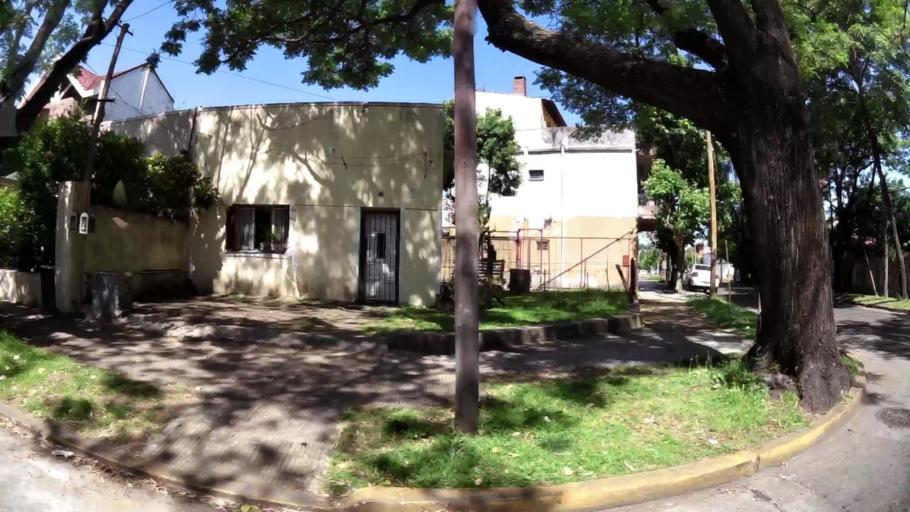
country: AR
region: Buenos Aires
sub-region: Partido de General San Martin
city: General San Martin
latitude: -34.5627
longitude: -58.5498
